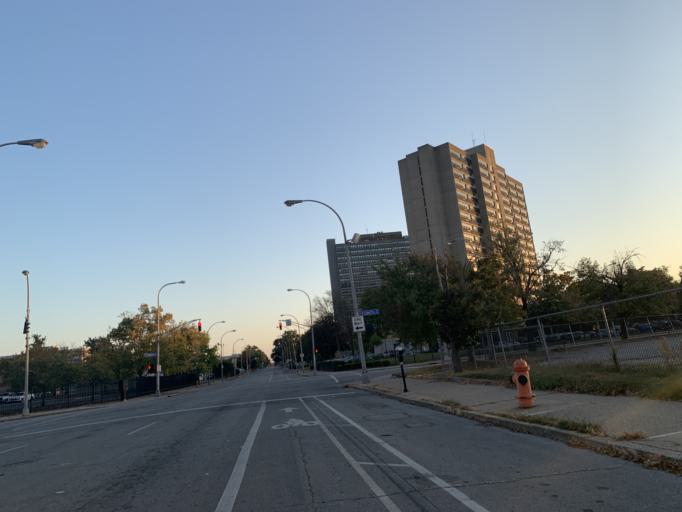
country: US
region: Kentucky
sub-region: Jefferson County
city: Louisville
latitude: 38.2538
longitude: -85.7638
